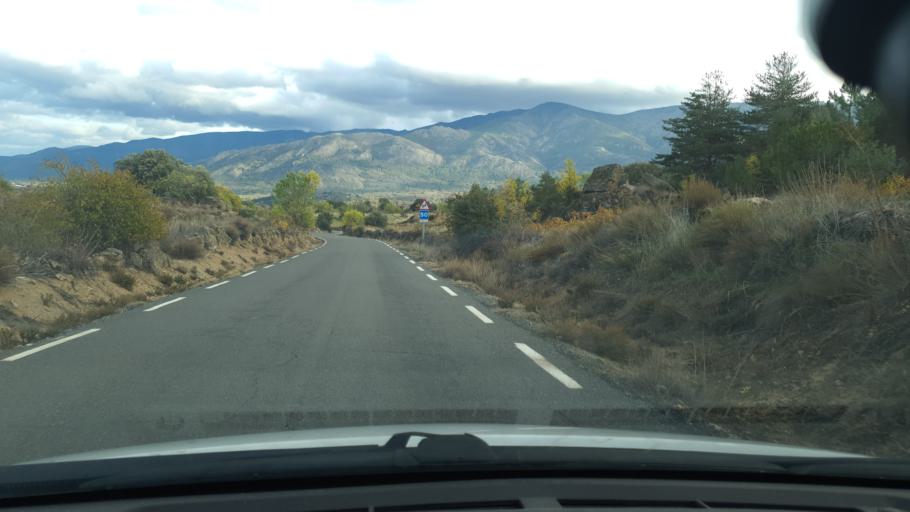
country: ES
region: Castille and Leon
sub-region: Provincia de Avila
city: Burgohondo
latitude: 40.4107
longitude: -4.8025
